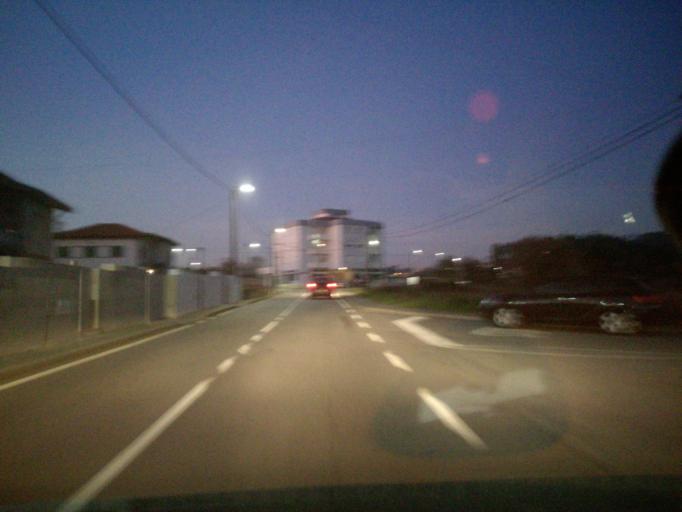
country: PT
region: Porto
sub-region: Maia
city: Nogueira
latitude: 41.2510
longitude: -8.5833
